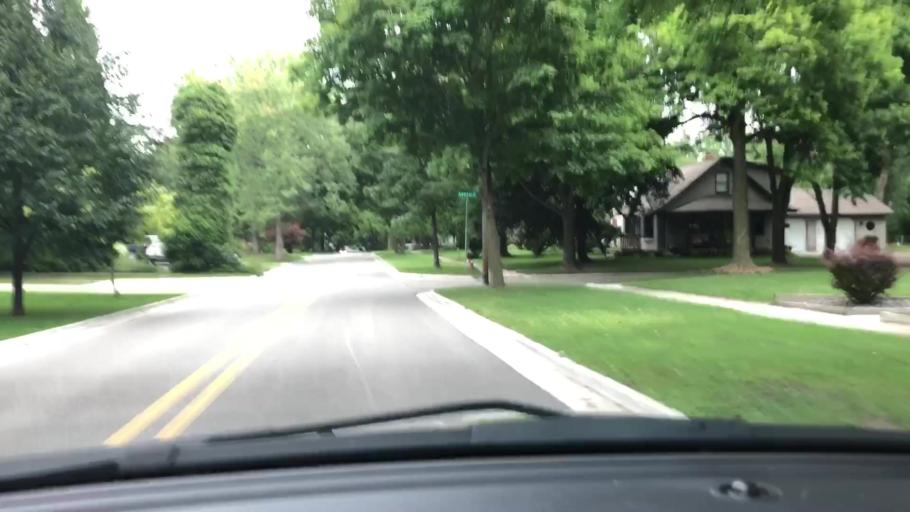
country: US
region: Michigan
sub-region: Midland County
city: Midland
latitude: 43.6319
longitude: -84.2319
